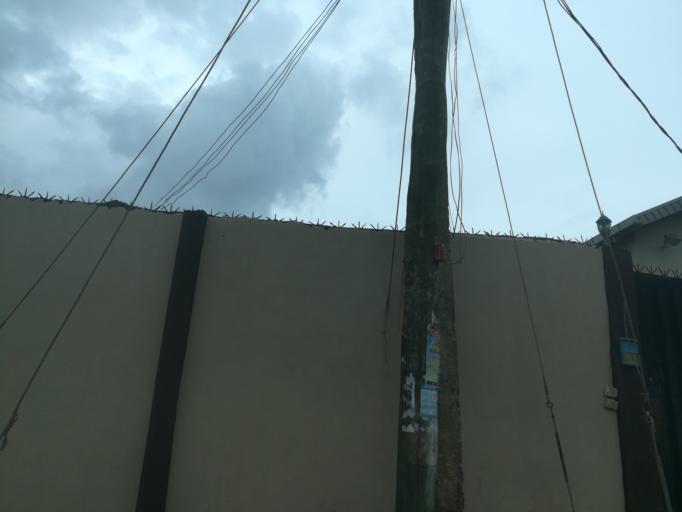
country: NG
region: Lagos
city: Agege
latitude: 6.6029
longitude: 3.3134
